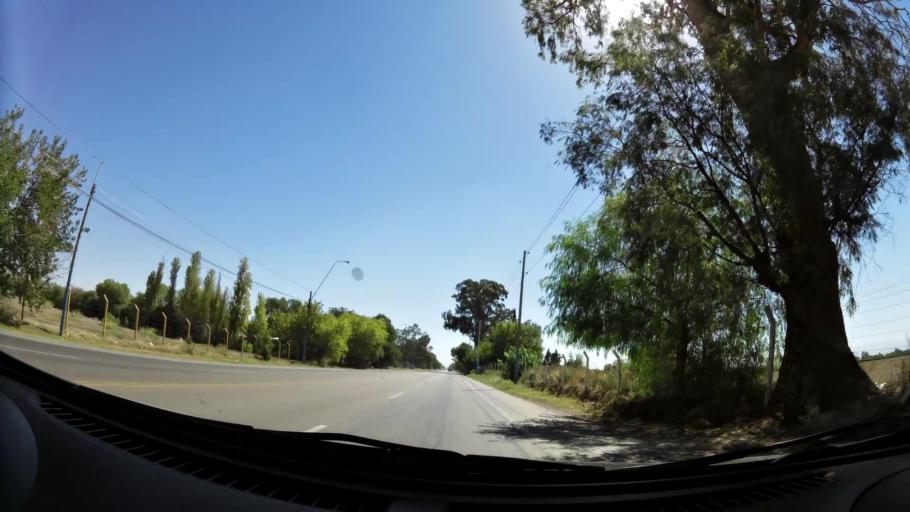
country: AR
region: San Juan
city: Villa Aberastain
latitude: -31.6177
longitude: -68.5491
